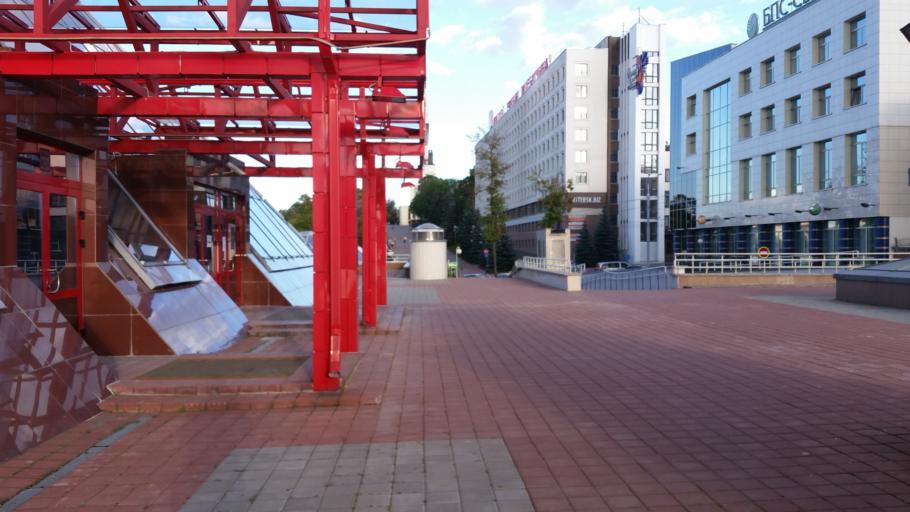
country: BY
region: Vitebsk
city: Vitebsk
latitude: 55.1911
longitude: 30.2047
